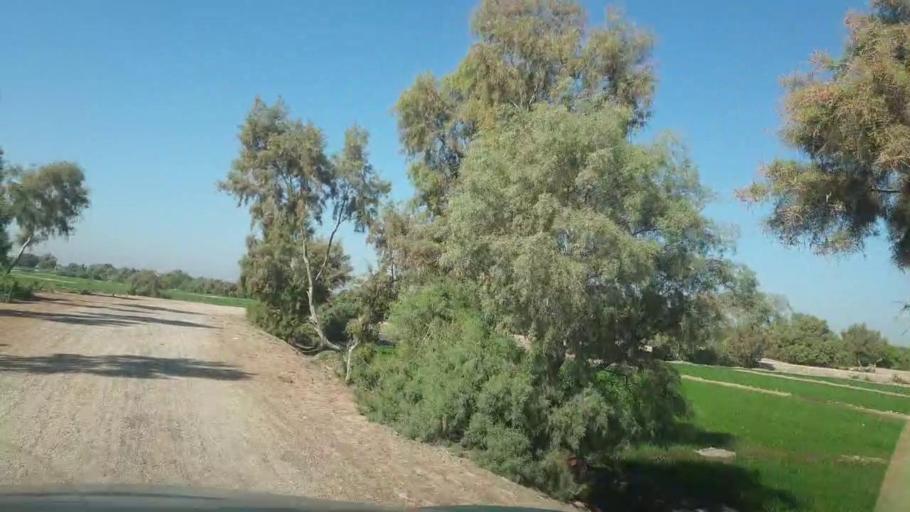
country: PK
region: Sindh
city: Bhan
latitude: 26.5282
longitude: 67.6434
